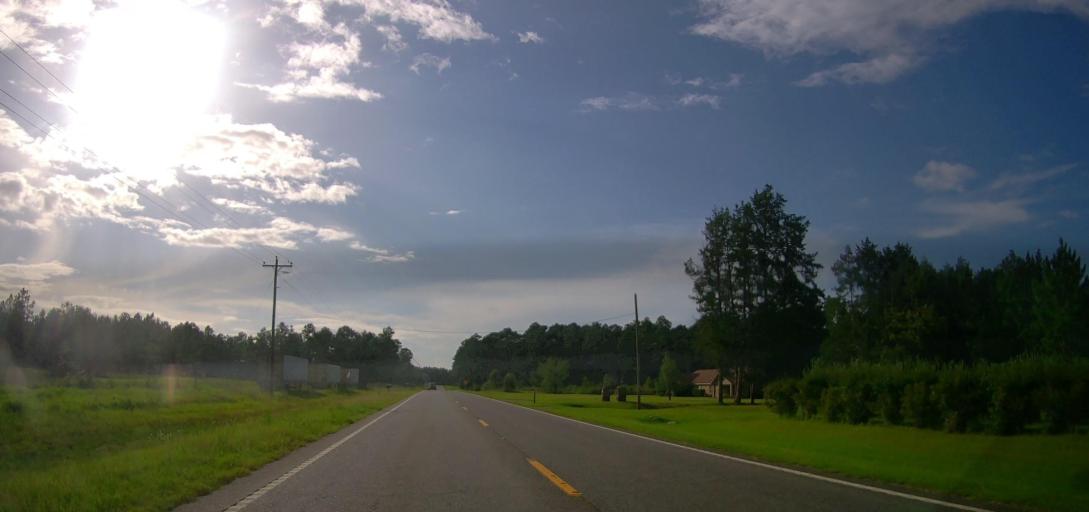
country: US
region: Georgia
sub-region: Coffee County
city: Nicholls
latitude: 31.3385
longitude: -82.6002
